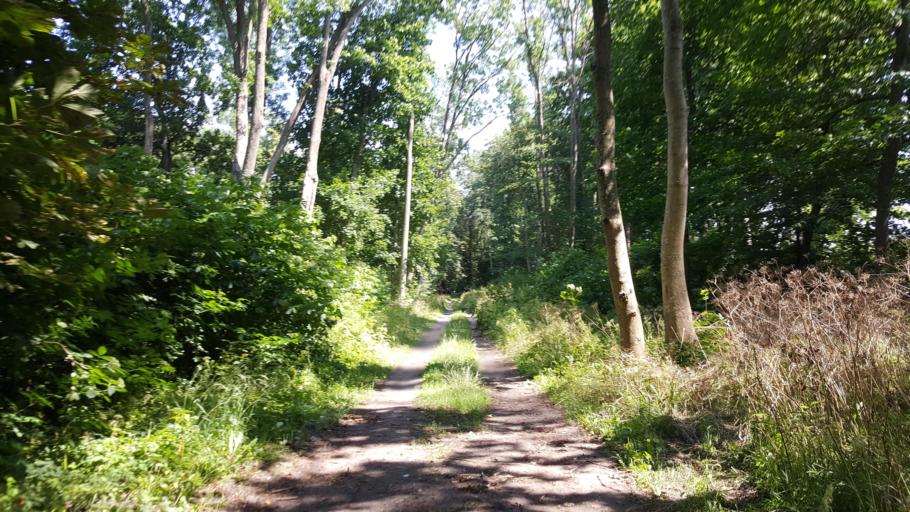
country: BY
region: Brest
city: Vysokaye
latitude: 52.3655
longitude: 23.3656
